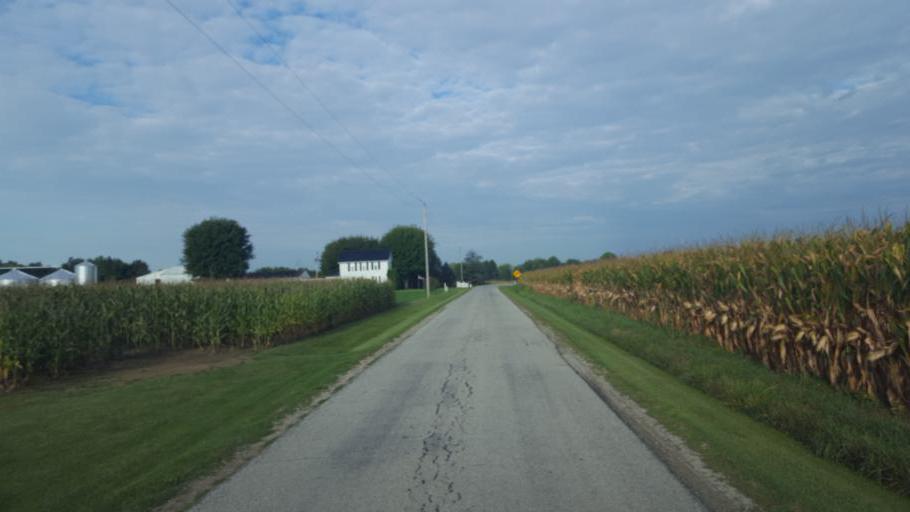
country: US
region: Ohio
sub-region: Morrow County
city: Mount Gilead
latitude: 40.6460
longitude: -82.9050
